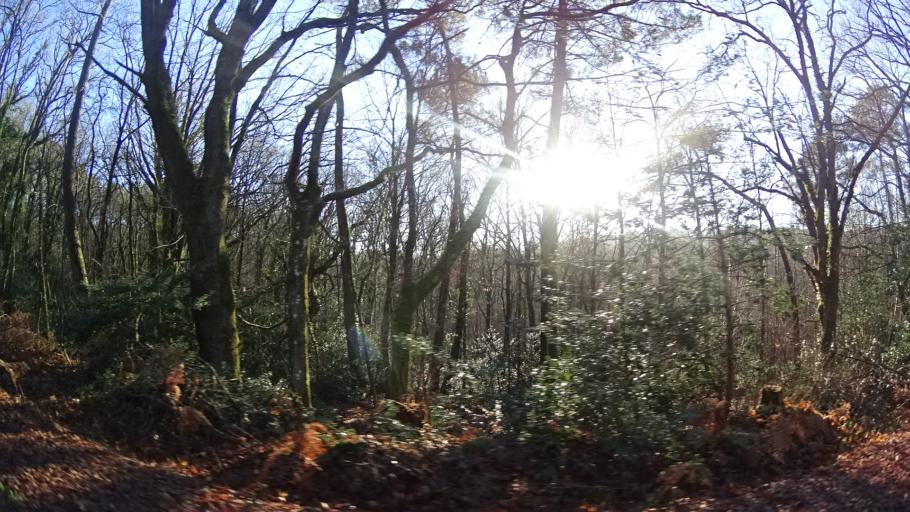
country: FR
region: Brittany
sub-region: Departement du Morbihan
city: Allaire
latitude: 47.6614
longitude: -2.1578
